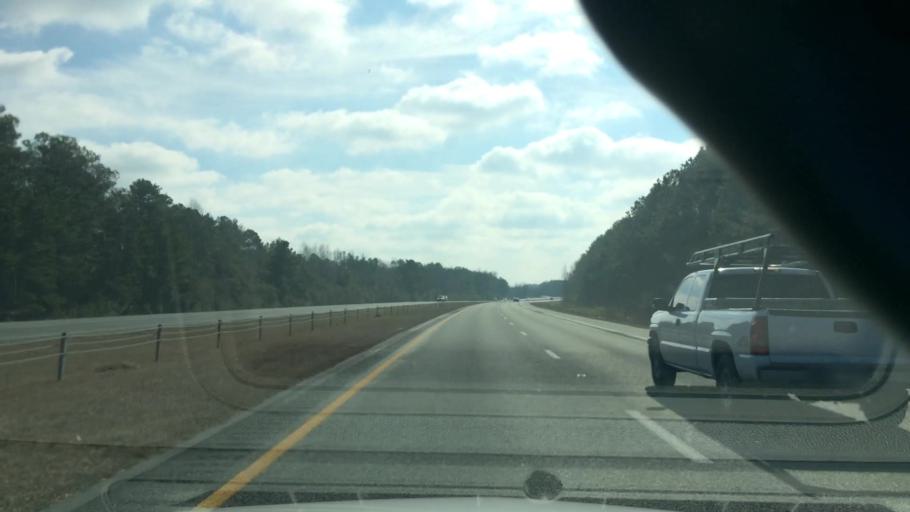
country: US
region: North Carolina
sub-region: Duplin County
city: Wallace
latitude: 34.6977
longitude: -77.9448
